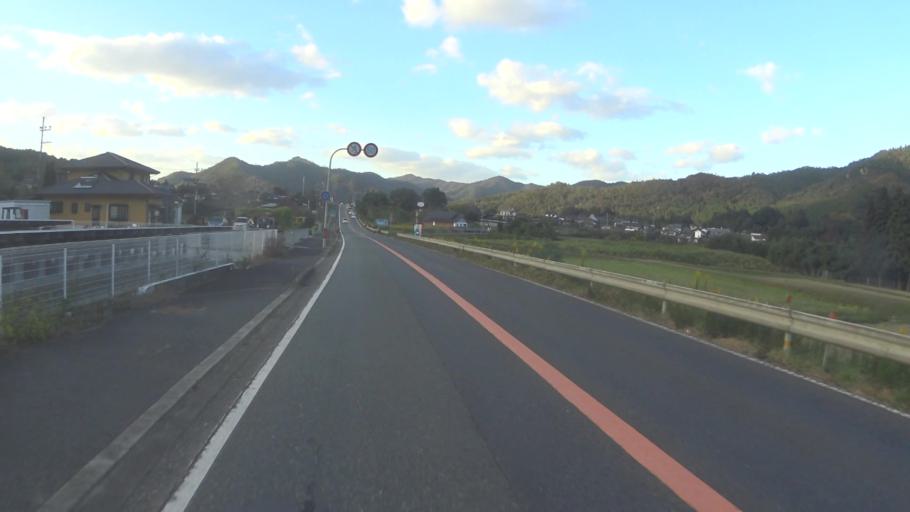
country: JP
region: Kyoto
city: Ayabe
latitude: 35.2423
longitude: 135.2176
